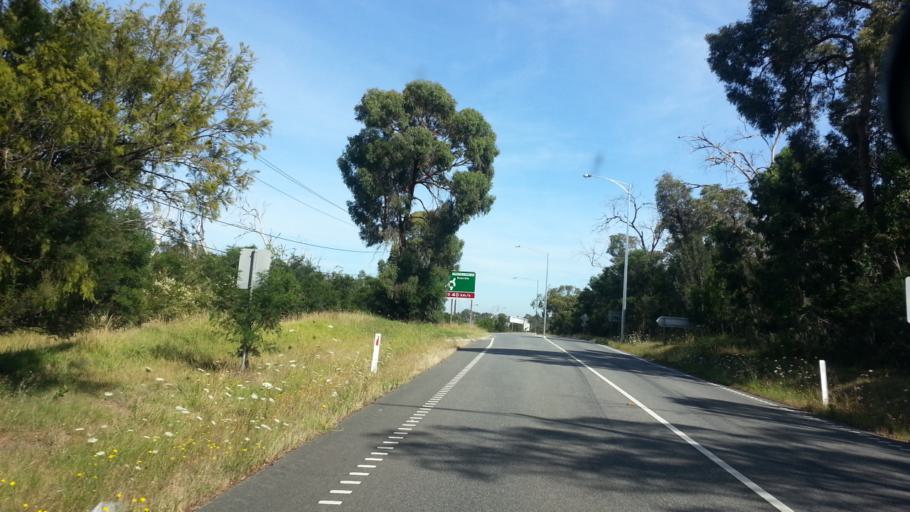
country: AU
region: Victoria
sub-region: Casey
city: Endeavour Hills
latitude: -37.9535
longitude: 145.2519
